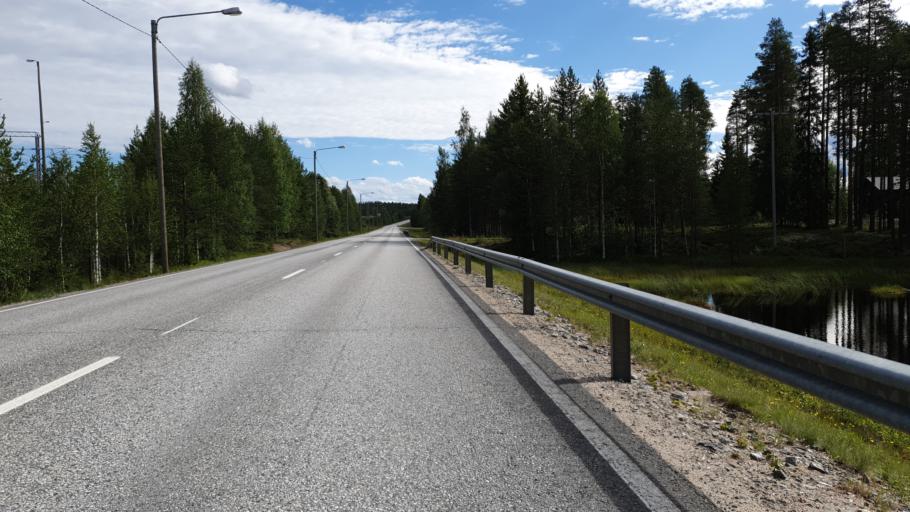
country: FI
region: Kainuu
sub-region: Kehys-Kainuu
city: Kuhmo
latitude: 64.5416
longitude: 29.9599
